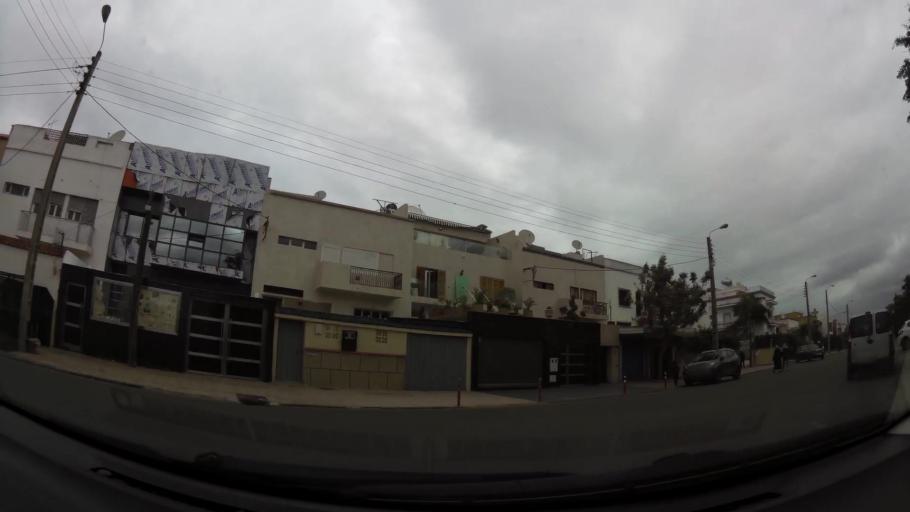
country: MA
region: Grand Casablanca
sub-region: Casablanca
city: Casablanca
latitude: 33.5728
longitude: -7.6691
